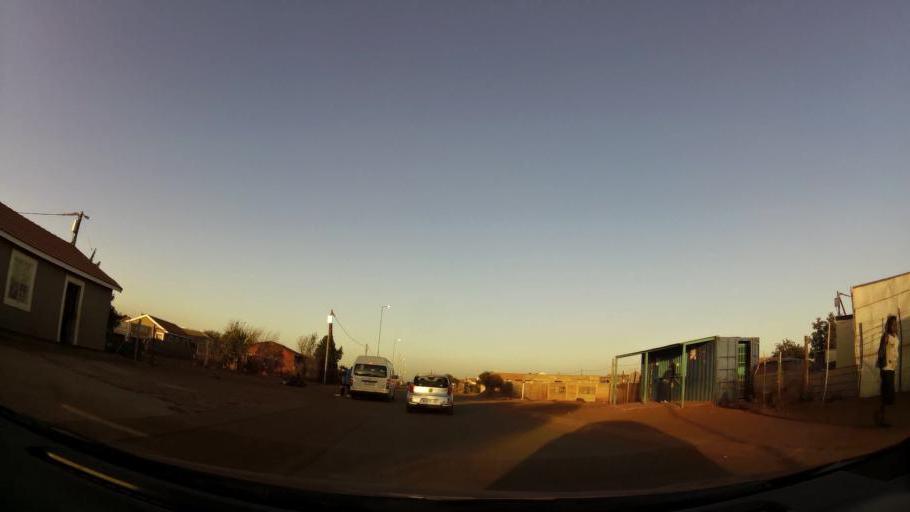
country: ZA
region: North-West
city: Ga-Rankuwa
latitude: -25.5958
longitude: 28.0898
